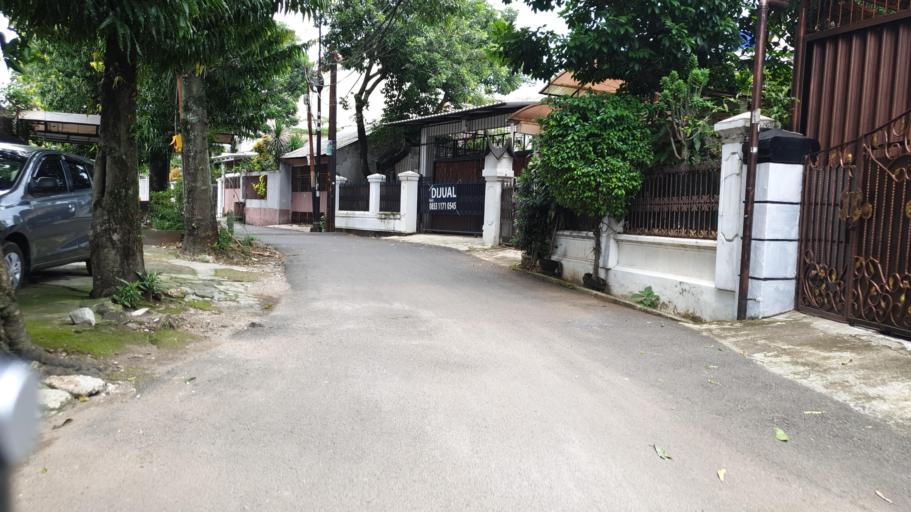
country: ID
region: West Java
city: Pamulang
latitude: -6.3054
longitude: 106.7804
